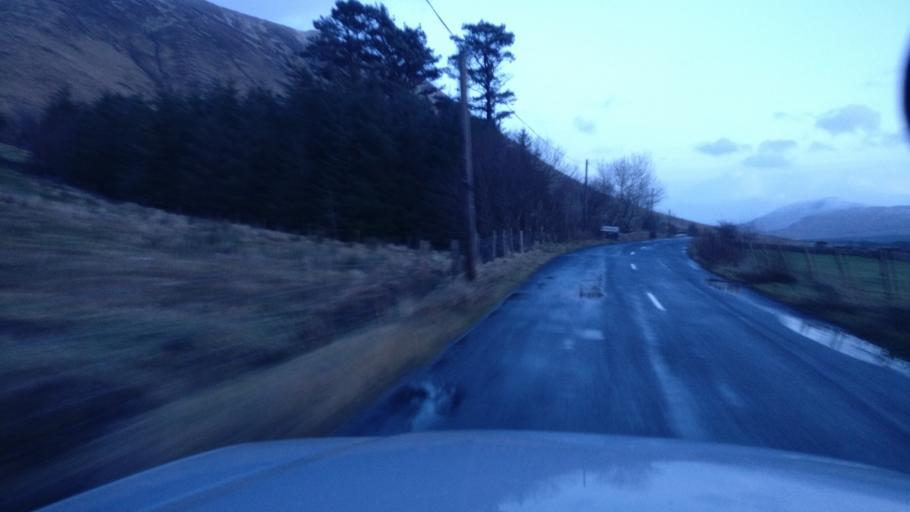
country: IE
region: Connaught
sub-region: Maigh Eo
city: Westport
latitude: 53.5715
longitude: -9.6584
